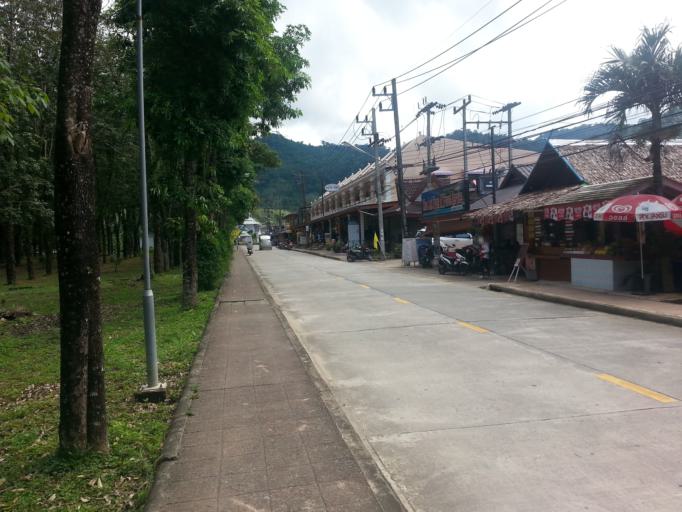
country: TH
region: Phangnga
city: Ban Khao Lak
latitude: 8.6452
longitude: 98.2488
